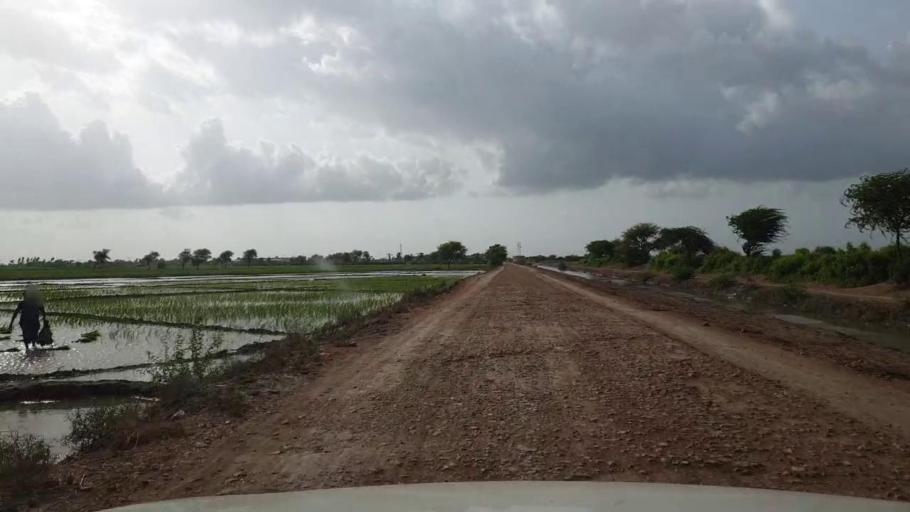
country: PK
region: Sindh
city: Kario
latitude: 24.7896
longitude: 68.5806
